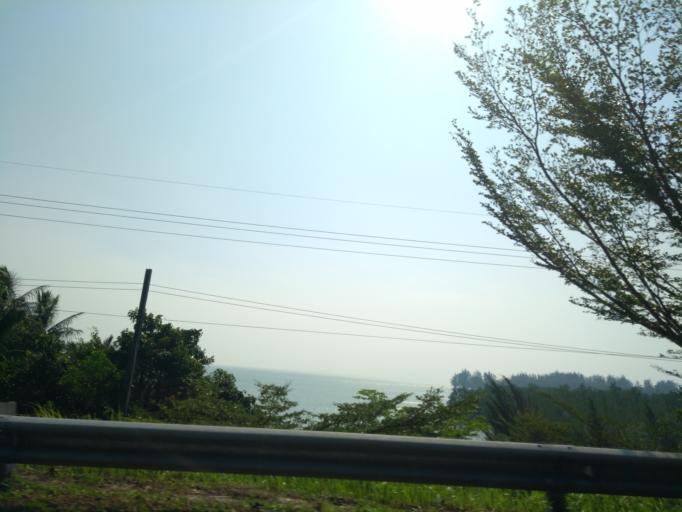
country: MY
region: Sarawak
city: Kuching
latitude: 1.7305
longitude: 110.3146
